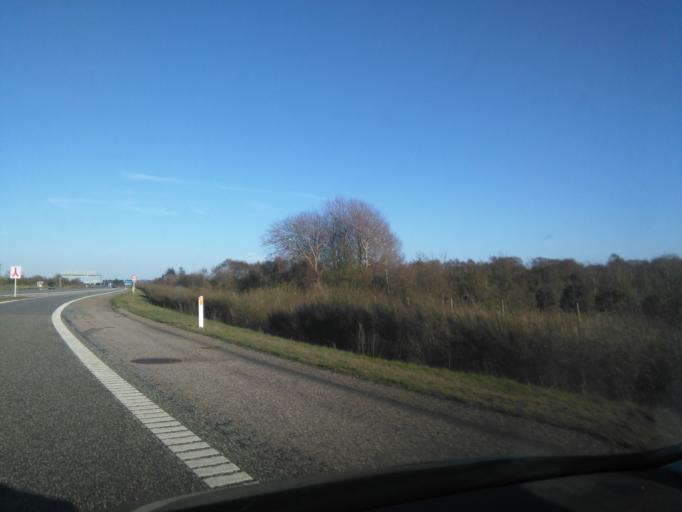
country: DK
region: Central Jutland
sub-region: Herning Kommune
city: Gjellerup Kirkeby
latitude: 56.1244
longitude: 9.0170
